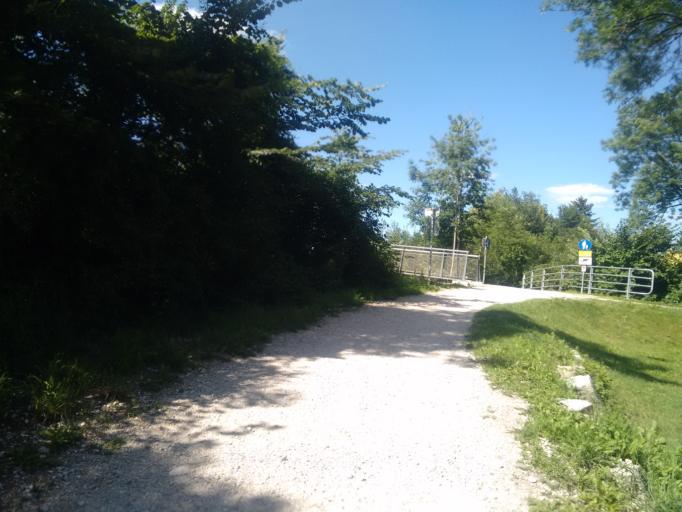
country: AT
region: Upper Austria
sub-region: Wels-Land
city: Thalheim bei Wels
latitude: 48.1482
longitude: 14.0179
